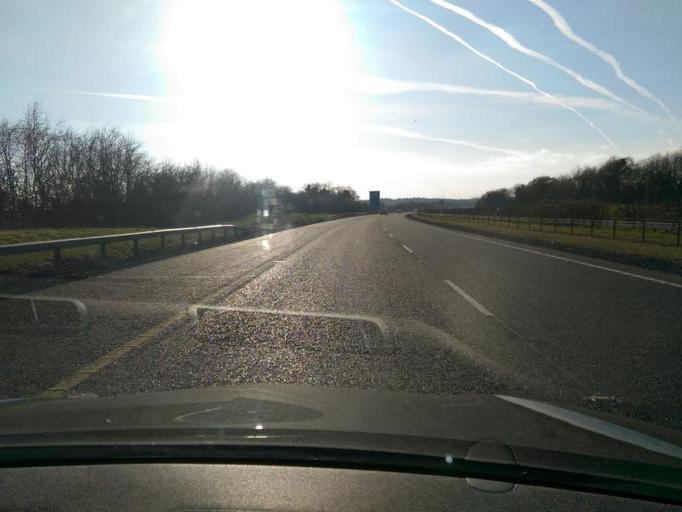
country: IE
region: Leinster
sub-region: Laois
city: Portlaoise
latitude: 53.0139
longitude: -7.2800
